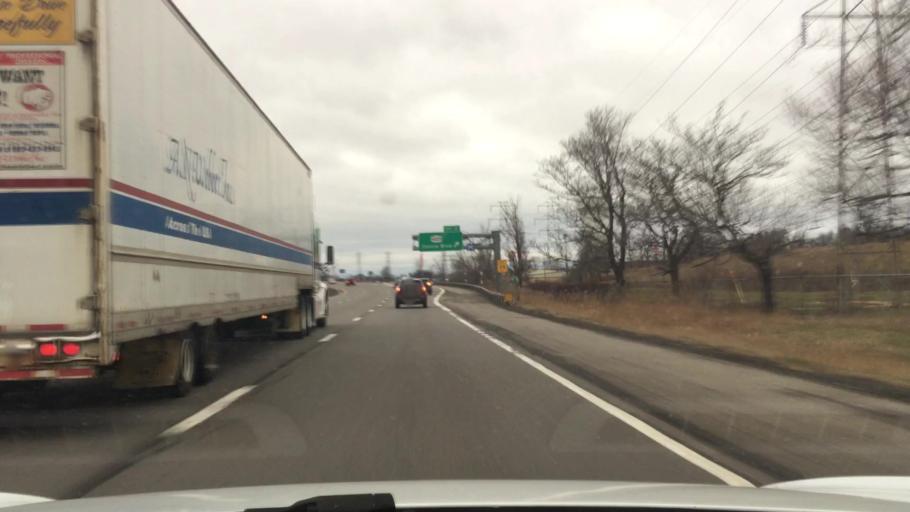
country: US
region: New York
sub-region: Erie County
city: Tonawanda
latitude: 43.0012
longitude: -78.8464
